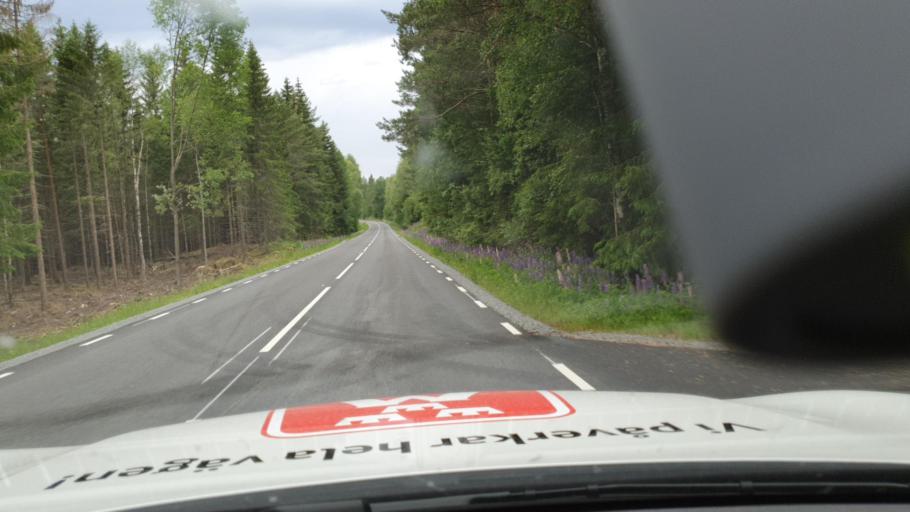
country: SE
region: OErebro
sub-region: Laxa Kommun
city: Laxa
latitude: 58.8972
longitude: 14.4838
